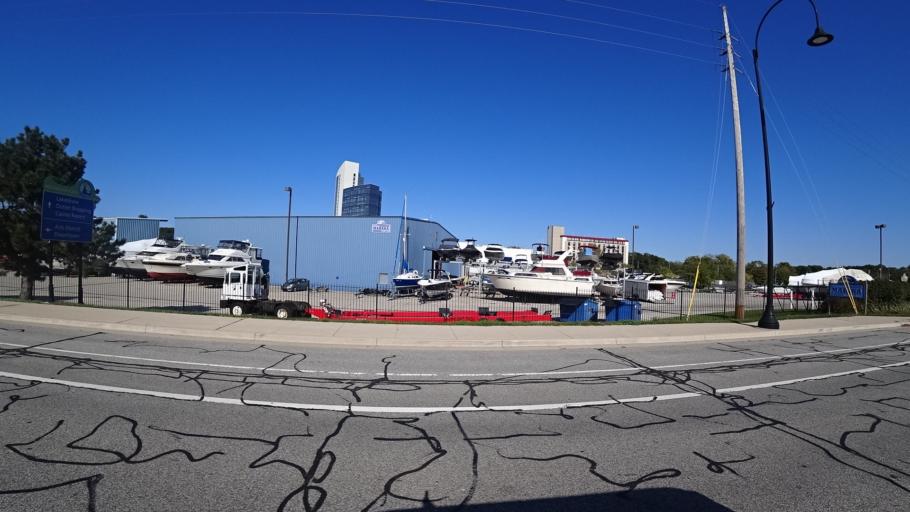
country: US
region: Indiana
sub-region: LaPorte County
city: Michigan City
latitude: 41.7172
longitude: -86.8945
